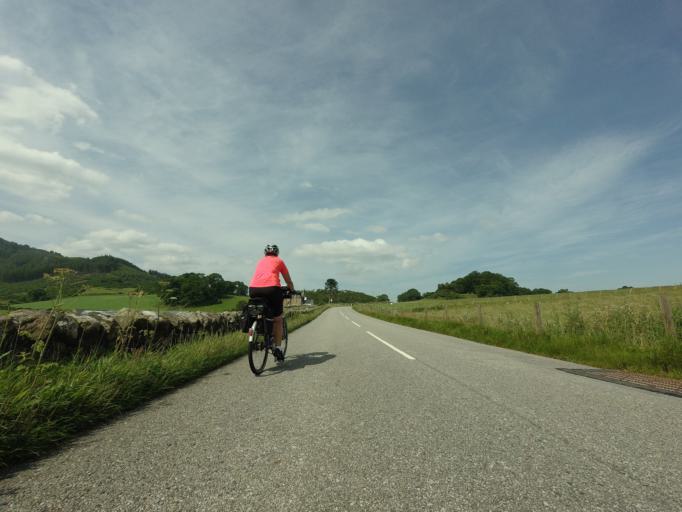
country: GB
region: Scotland
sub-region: Highland
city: Tain
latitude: 57.8485
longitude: -4.2023
